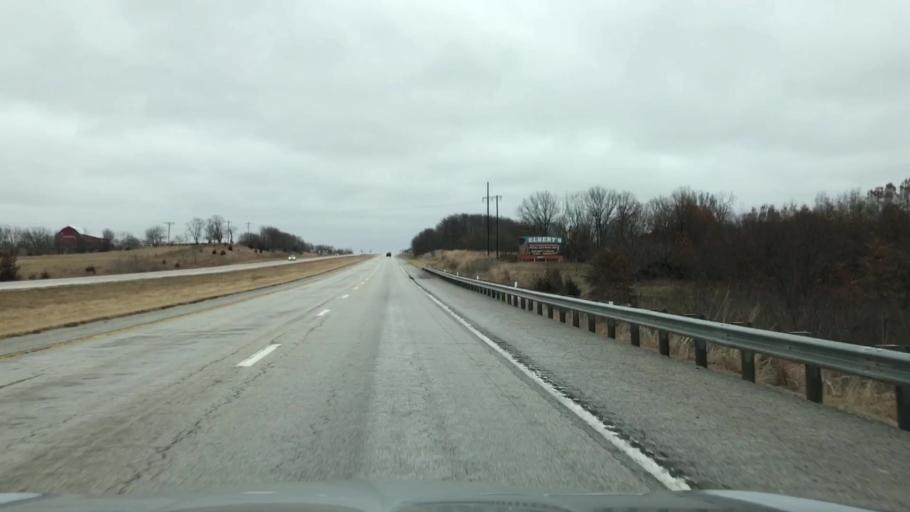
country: US
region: Missouri
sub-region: Caldwell County
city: Hamilton
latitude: 39.7503
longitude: -94.1180
